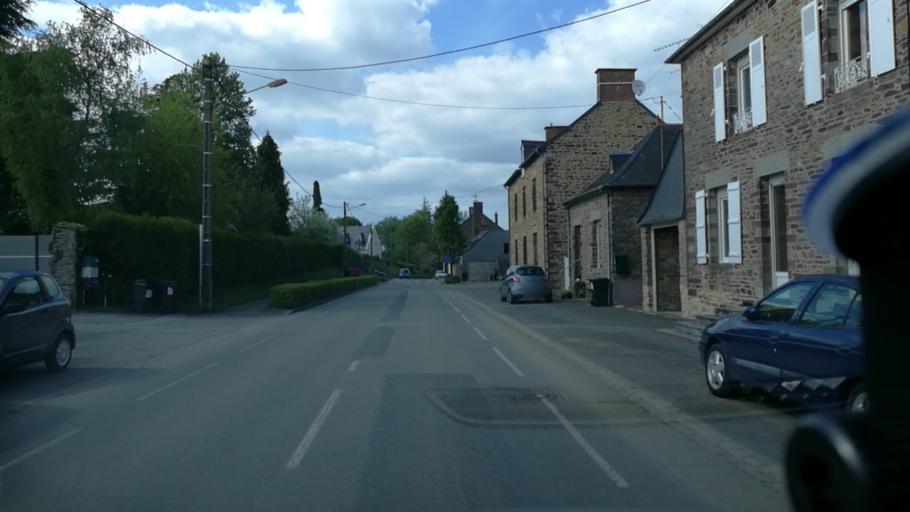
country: FR
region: Brittany
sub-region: Departement d'Ille-et-Vilaine
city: Retiers
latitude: 47.9076
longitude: -1.3763
